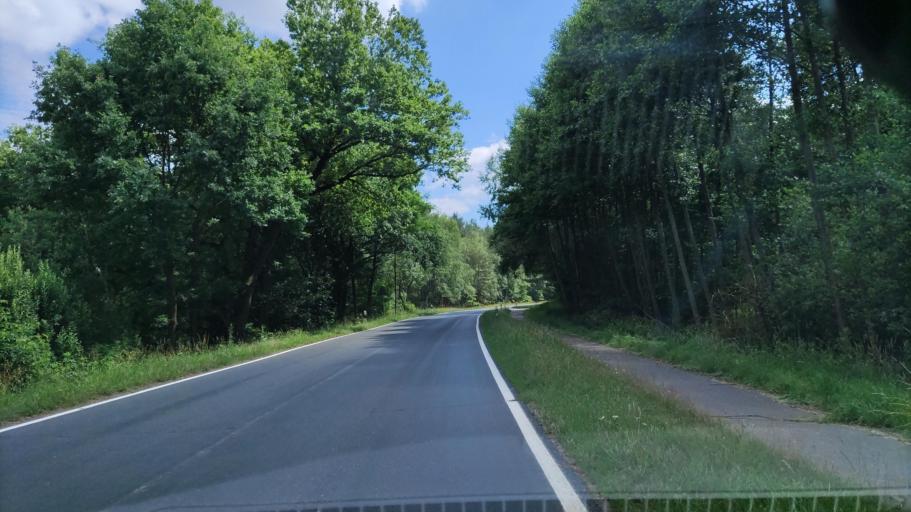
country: DE
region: Mecklenburg-Vorpommern
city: Lubtheen
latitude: 53.3344
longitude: 11.1312
